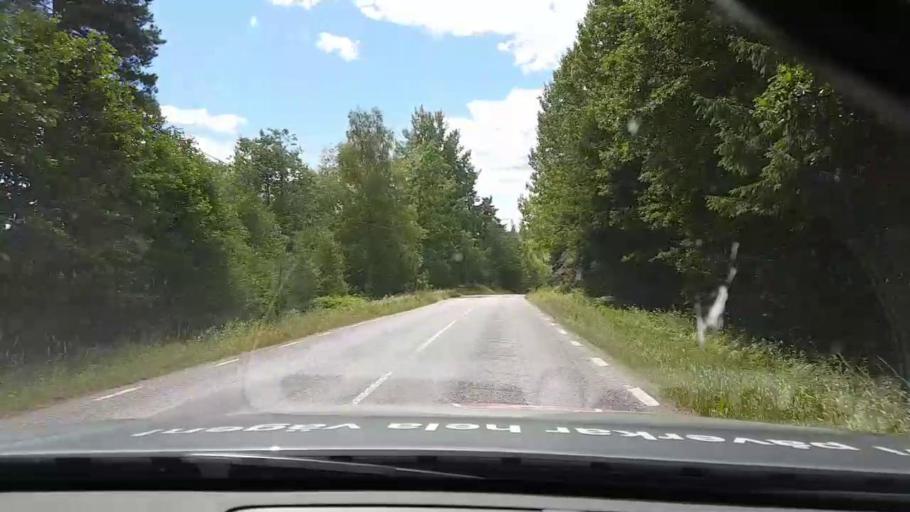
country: SE
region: Kalmar
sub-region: Vasterviks Kommun
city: Forserum
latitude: 58.0236
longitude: 16.5325
